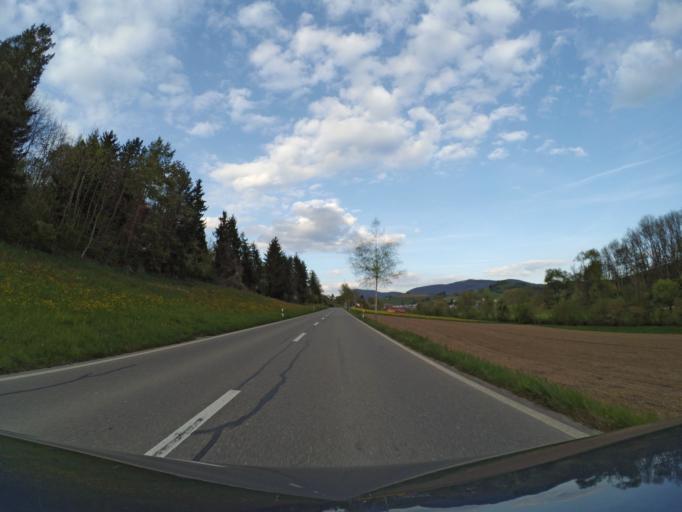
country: CH
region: Schaffhausen
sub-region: Bezirk Schleitheim
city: Schleitheim
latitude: 47.7470
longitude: 8.4694
